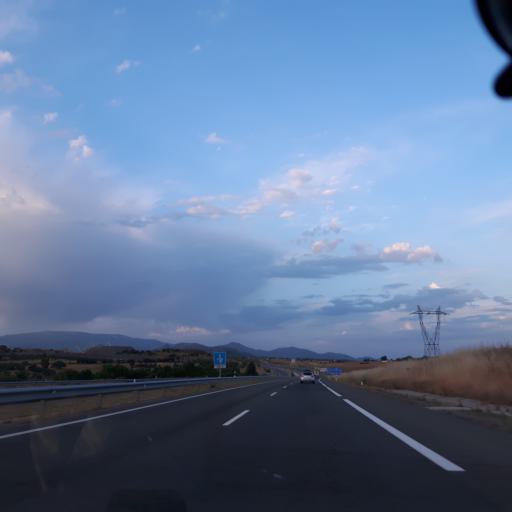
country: ES
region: Castille and Leon
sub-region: Provincia de Salamanca
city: Guijuelo
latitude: 40.5326
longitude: -5.6670
